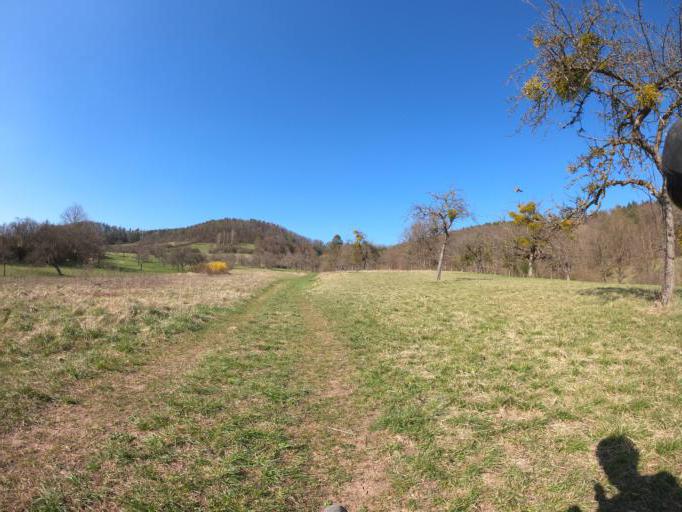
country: DE
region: Baden-Wuerttemberg
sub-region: Tuebingen Region
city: Rottenburg
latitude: 48.4430
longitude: 8.9350
